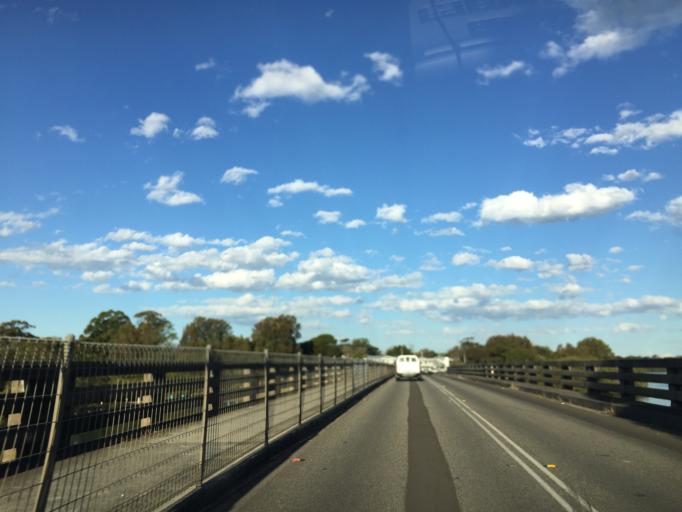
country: AU
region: New South Wales
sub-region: Shellharbour
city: Croom
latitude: -34.6214
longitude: 150.8456
